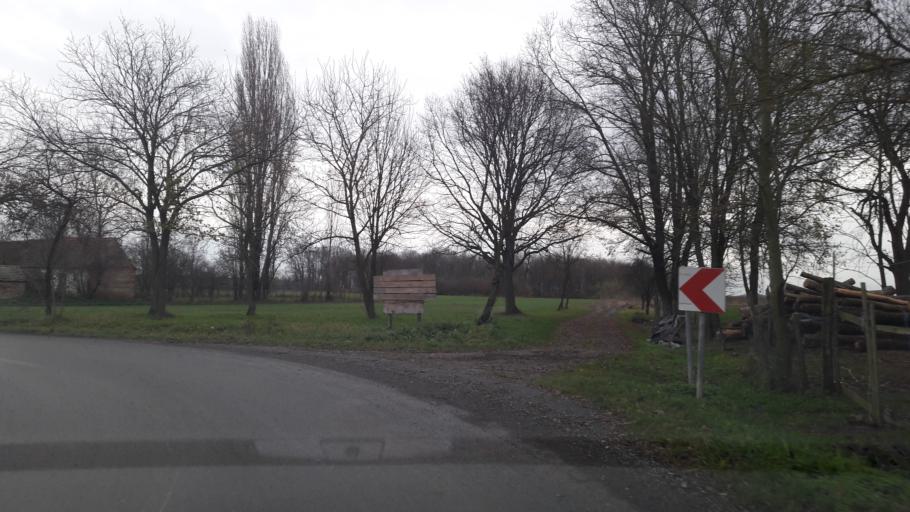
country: HR
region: Virovitick-Podravska
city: Zdenci
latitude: 45.6046
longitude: 18.0100
